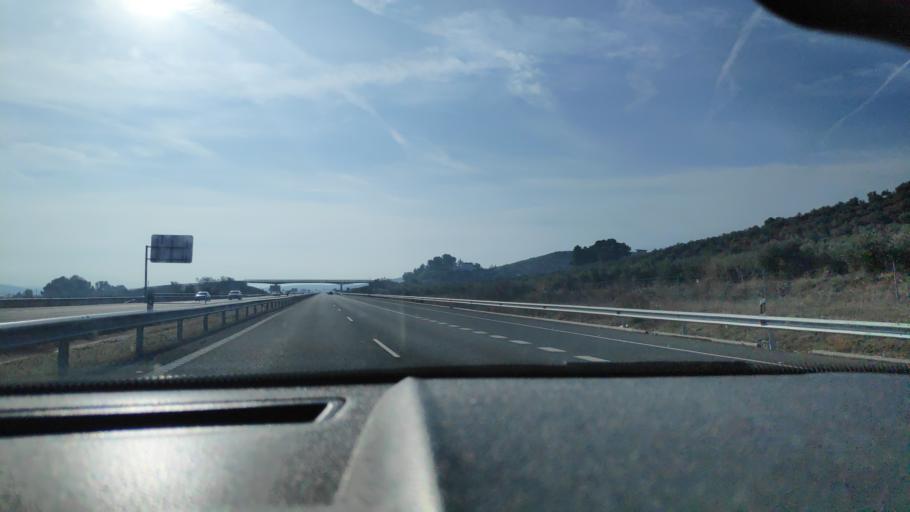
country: ES
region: Andalusia
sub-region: Provincia de Jaen
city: Mengibar
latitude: 37.9053
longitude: -3.7830
